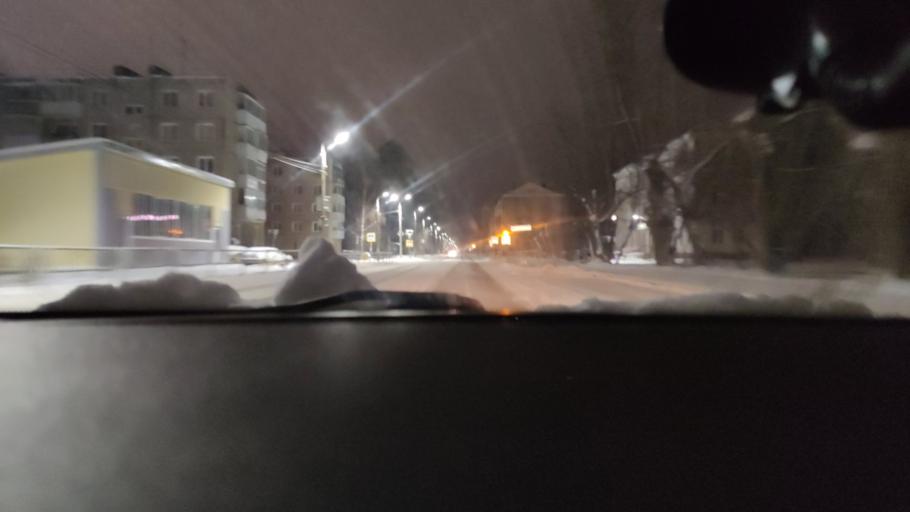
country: RU
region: Perm
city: Krasnokamsk
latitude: 58.0867
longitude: 55.7523
